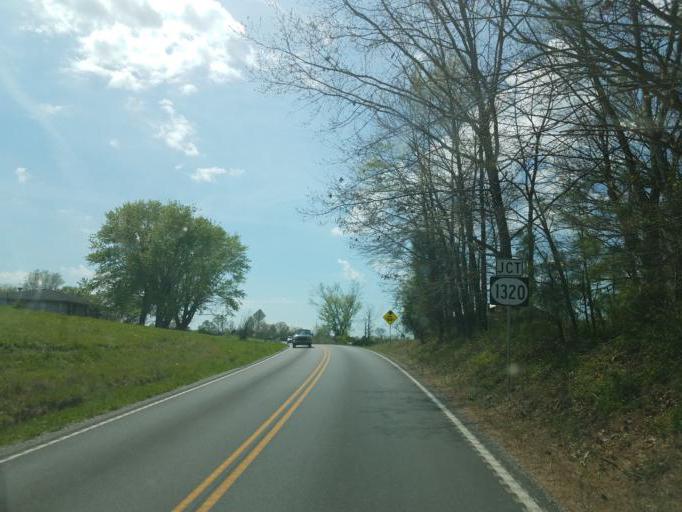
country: US
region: Kentucky
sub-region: Warren County
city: Bowling Green
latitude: 37.1146
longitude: -86.4242
